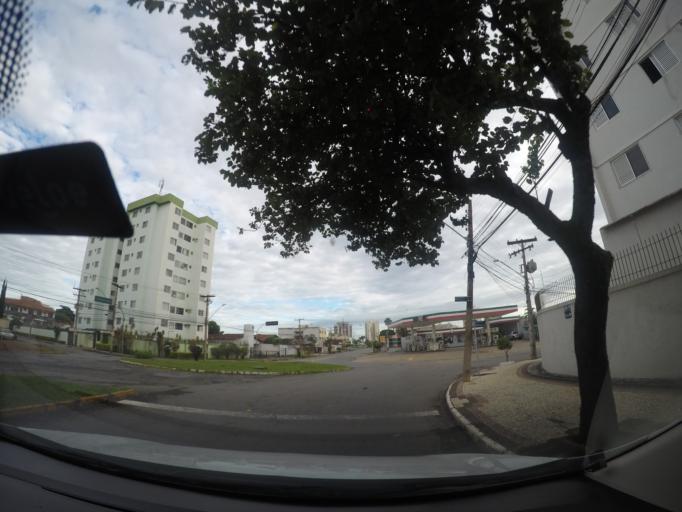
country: BR
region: Goias
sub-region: Goiania
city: Goiania
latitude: -16.6836
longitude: -49.2771
